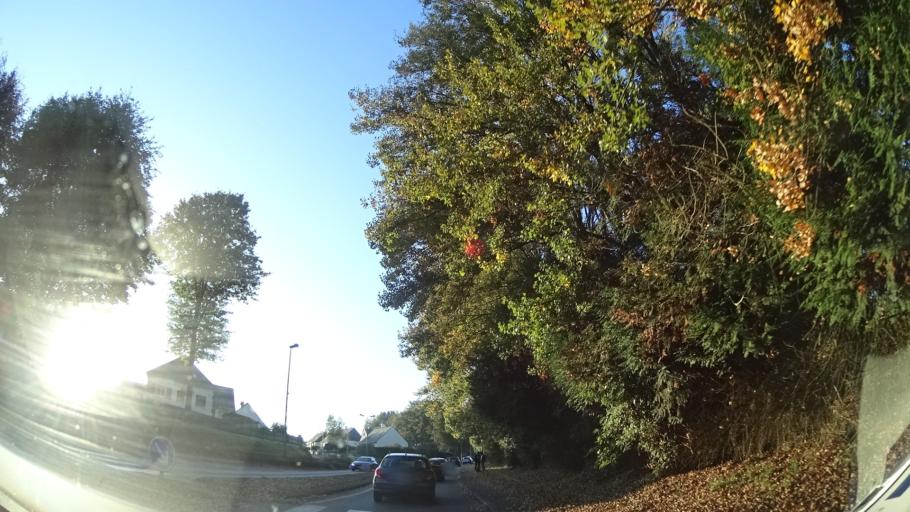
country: FR
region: Brittany
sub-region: Departement d'Ille-et-Vilaine
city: Geveze
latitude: 48.2185
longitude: -1.7835
